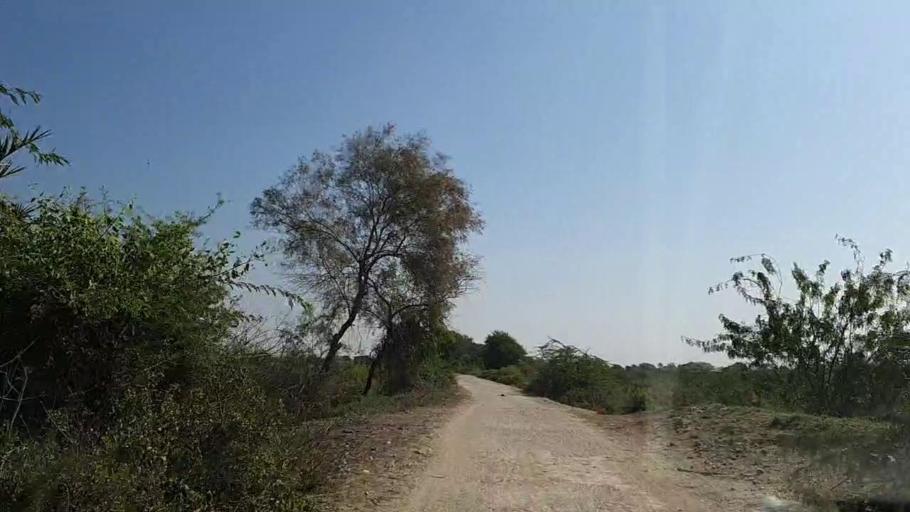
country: PK
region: Sindh
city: Chuhar Jamali
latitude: 24.4617
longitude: 68.1080
